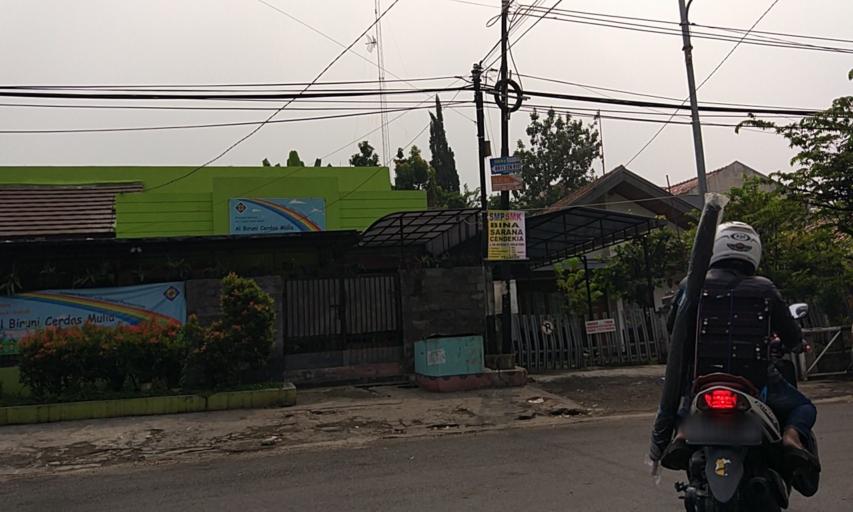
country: ID
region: West Java
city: Bandung
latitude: -6.8936
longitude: 107.6306
